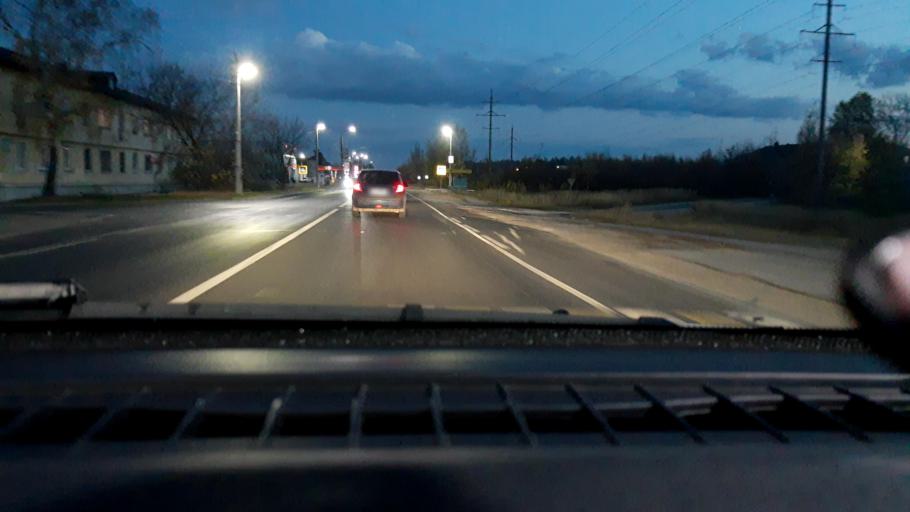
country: RU
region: Nizjnij Novgorod
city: Novaya Balakhna
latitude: 56.4802
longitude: 43.6037
